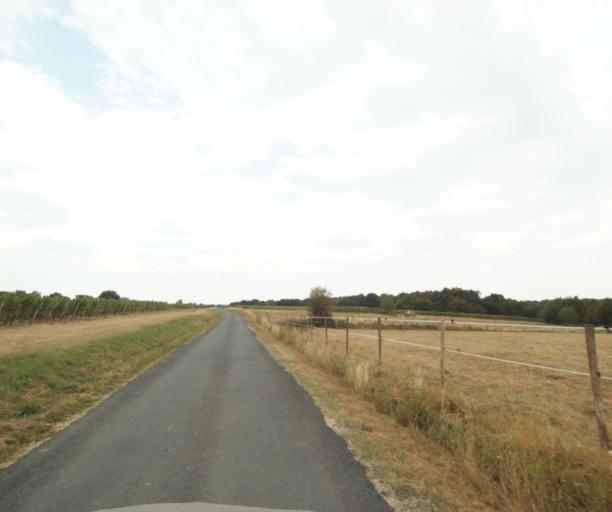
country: FR
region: Aquitaine
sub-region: Departement de la Gironde
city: Creon
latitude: 44.7511
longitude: -0.3379
